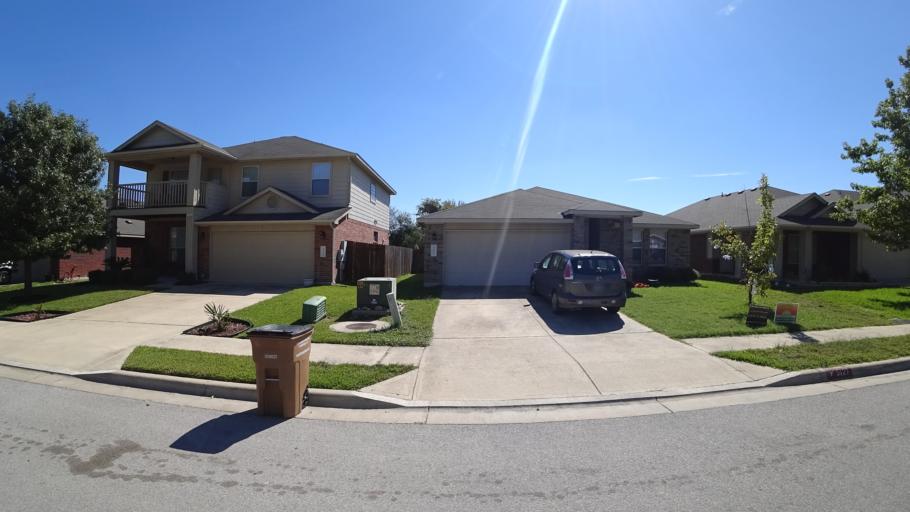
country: US
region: Texas
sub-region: Travis County
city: Hornsby Bend
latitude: 30.2730
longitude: -97.6316
